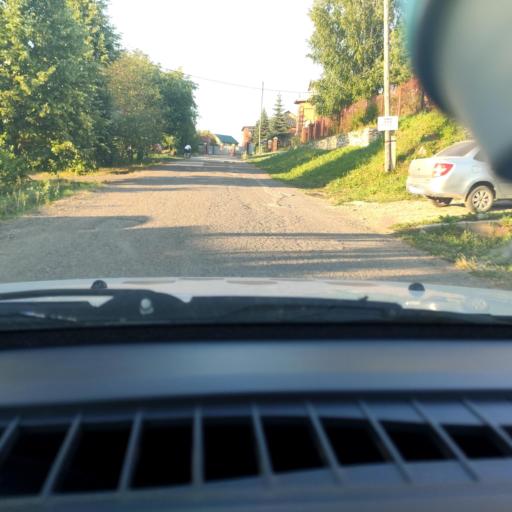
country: RU
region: Perm
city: Kungur
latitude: 57.4383
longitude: 57.0173
